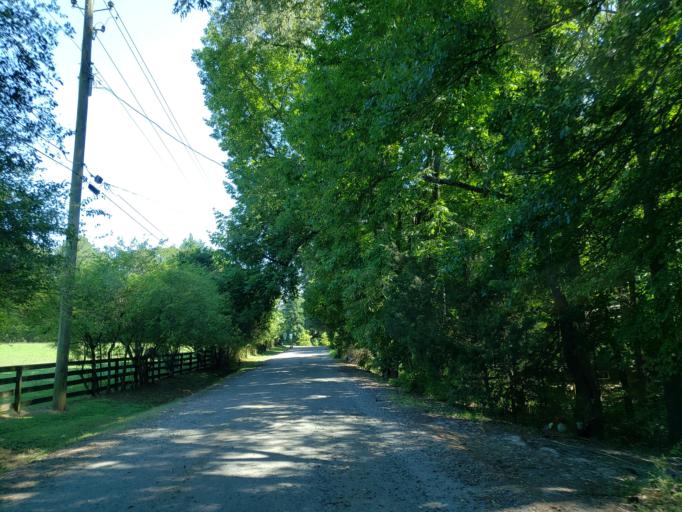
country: US
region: Georgia
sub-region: Fulton County
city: Milton
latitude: 34.1169
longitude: -84.3109
